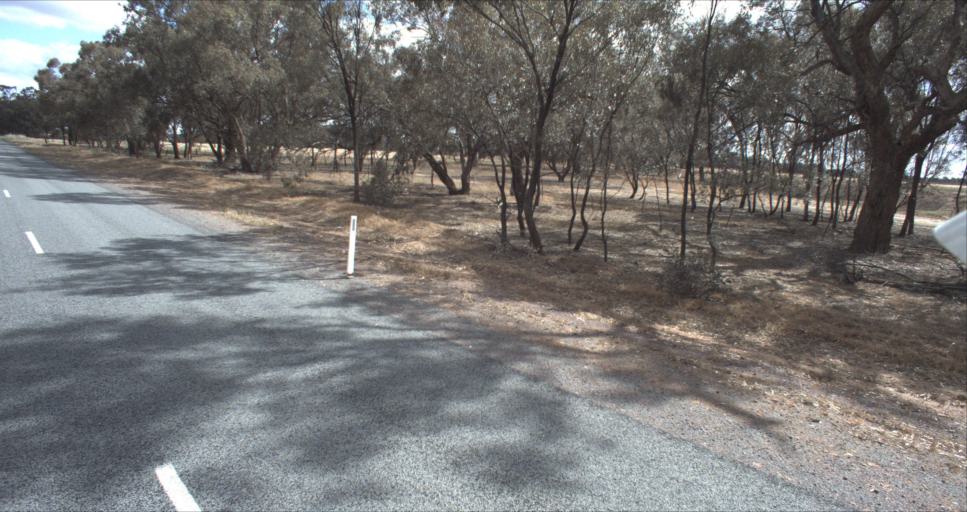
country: AU
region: New South Wales
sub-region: Leeton
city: Leeton
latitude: -34.6645
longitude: 146.3487
